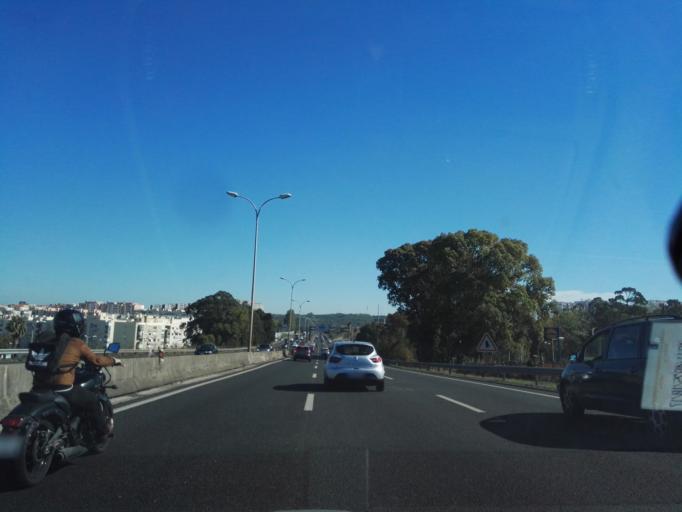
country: PT
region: Lisbon
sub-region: Amadora
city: Amadora
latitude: 38.7419
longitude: -9.2255
